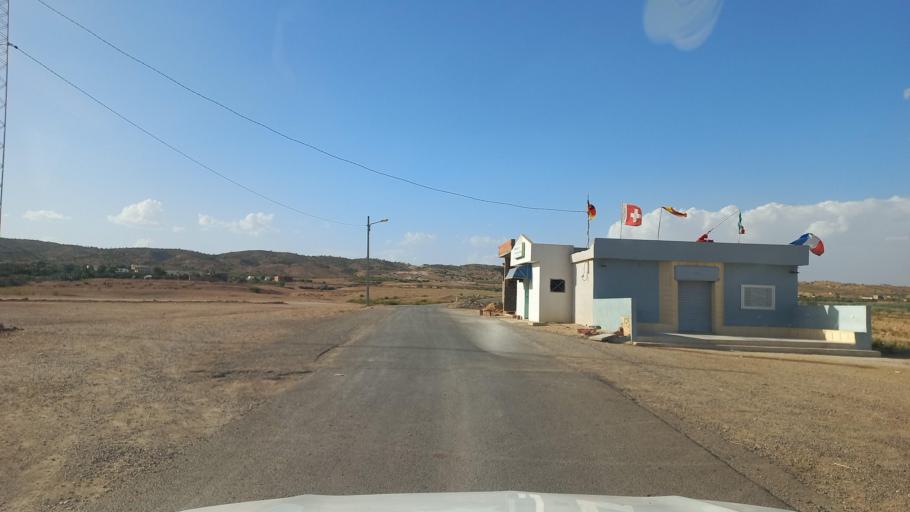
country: TN
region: Al Qasrayn
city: Sbiba
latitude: 35.3445
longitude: 8.9904
